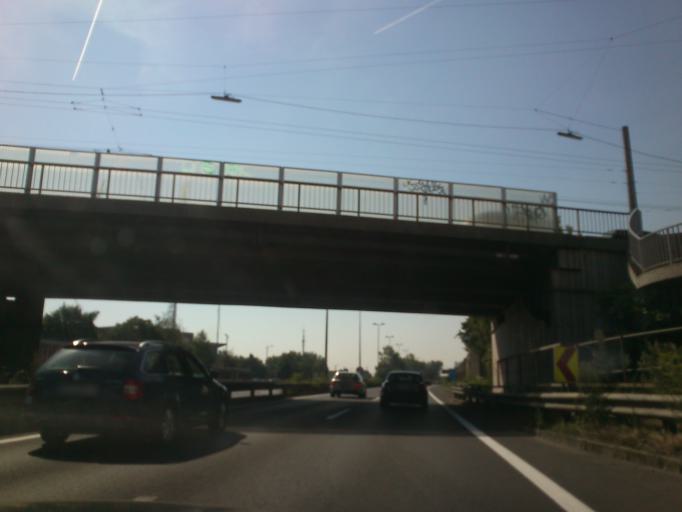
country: AT
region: Upper Austria
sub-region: Linz Stadt
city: Linz
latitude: 48.3090
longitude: 14.3116
